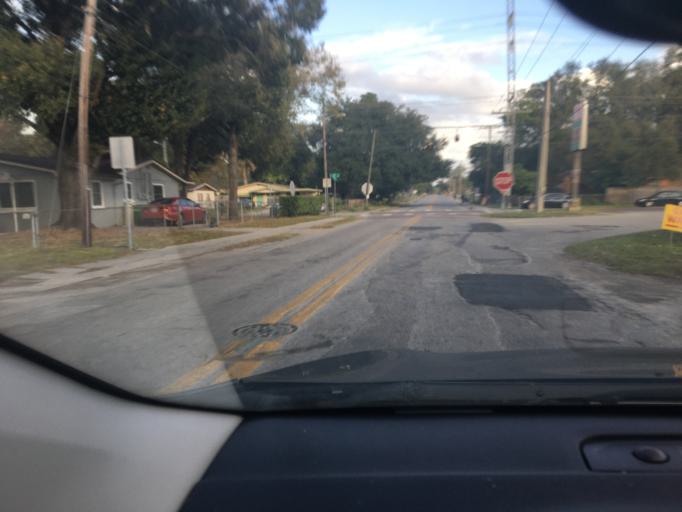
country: US
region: Florida
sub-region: Hillsborough County
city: University
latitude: 28.0399
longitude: -82.4352
